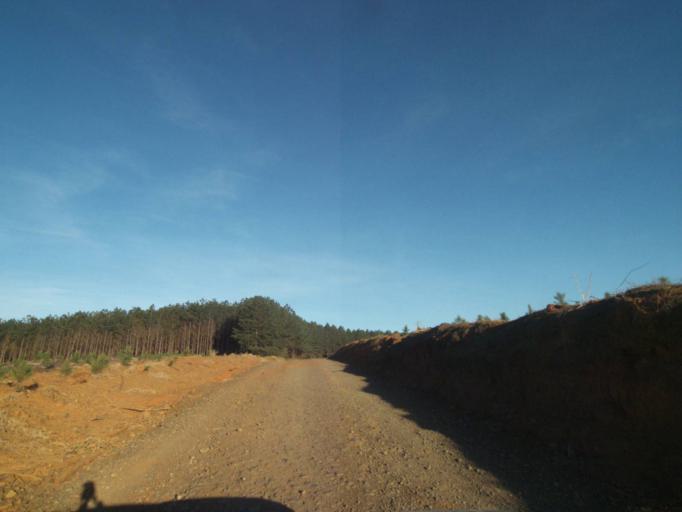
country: BR
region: Parana
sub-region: Telemaco Borba
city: Telemaco Borba
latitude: -24.4458
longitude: -50.5987
